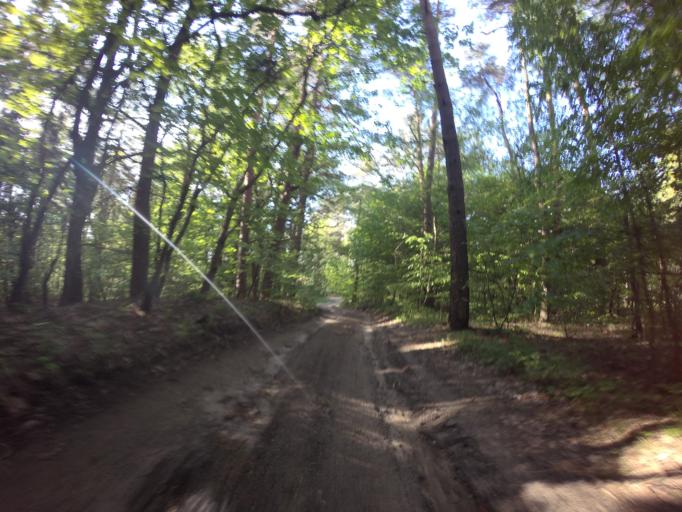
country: PL
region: West Pomeranian Voivodeship
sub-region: Powiat choszczenski
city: Drawno
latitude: 53.2110
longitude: 15.7303
